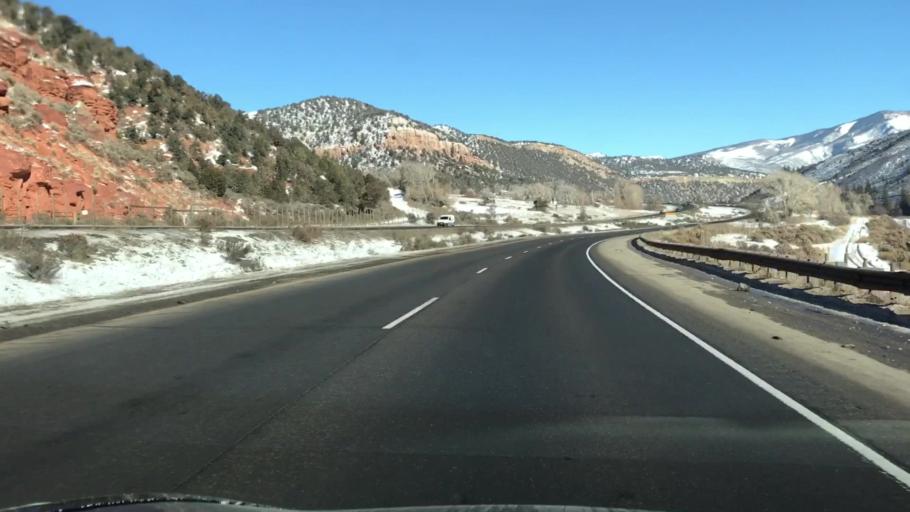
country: US
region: Colorado
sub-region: Eagle County
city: Eagle
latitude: 39.7051
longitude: -106.7274
